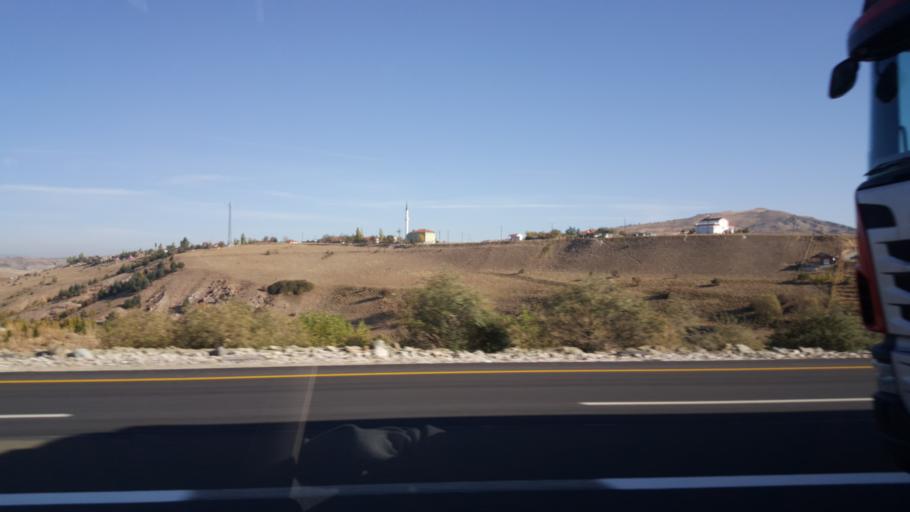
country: TR
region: Ankara
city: Mamak
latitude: 39.9826
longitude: 32.9570
